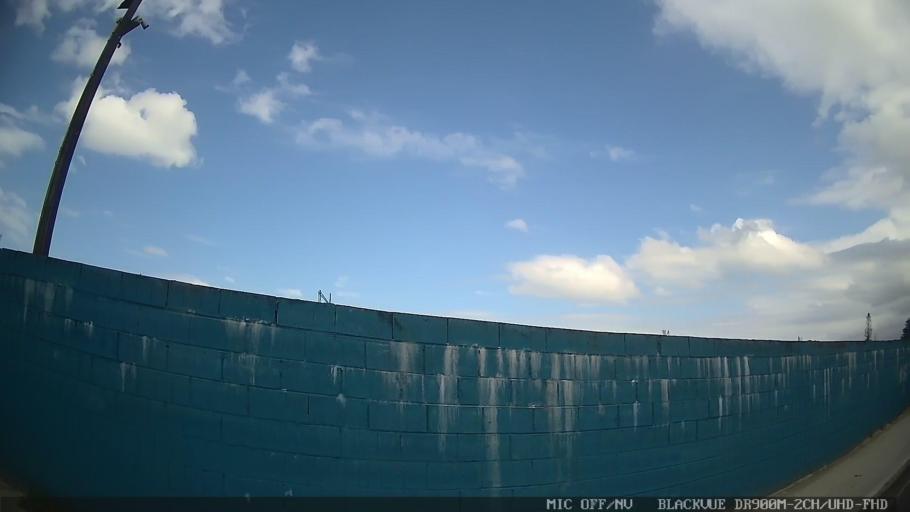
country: BR
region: Sao Paulo
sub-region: Guaruja
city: Guaruja
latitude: -23.9984
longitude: -46.2871
